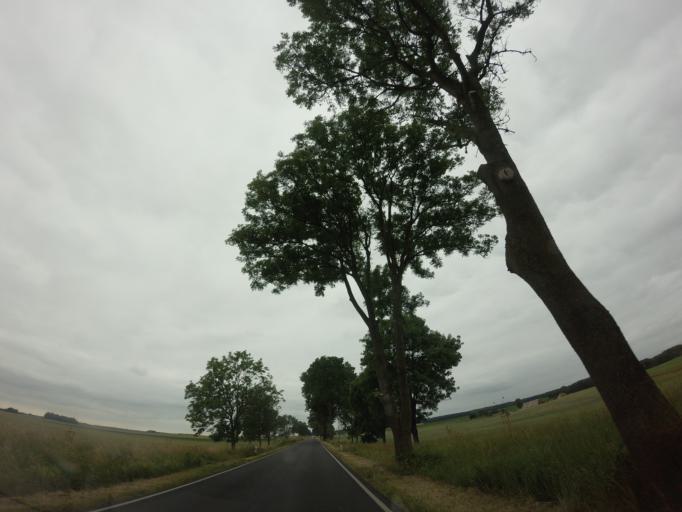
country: PL
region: West Pomeranian Voivodeship
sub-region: Powiat choszczenski
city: Recz
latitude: 53.1890
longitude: 15.5722
